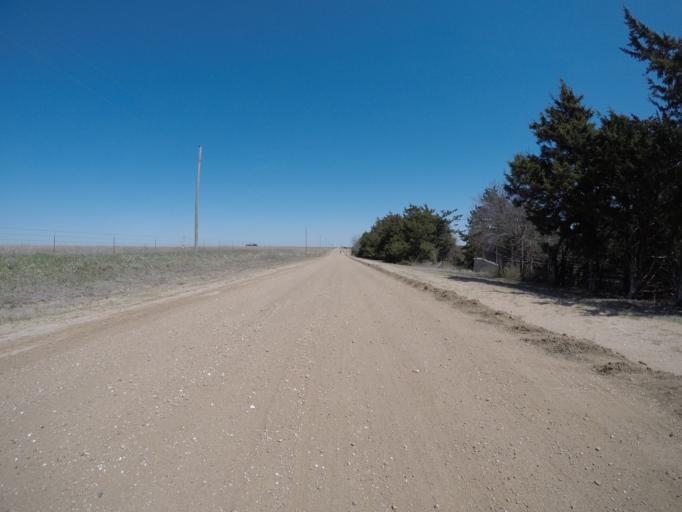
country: US
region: Kansas
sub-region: Pratt County
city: Pratt
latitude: 37.4214
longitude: -98.8388
